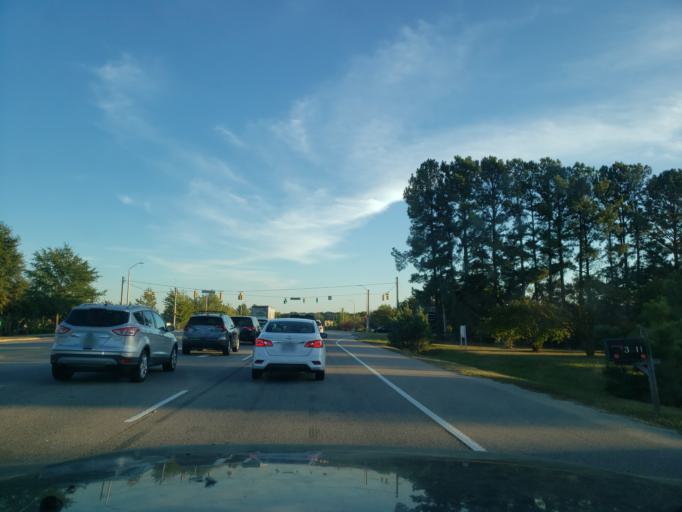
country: US
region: North Carolina
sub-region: Wake County
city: Morrisville
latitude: 35.8235
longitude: -78.8486
